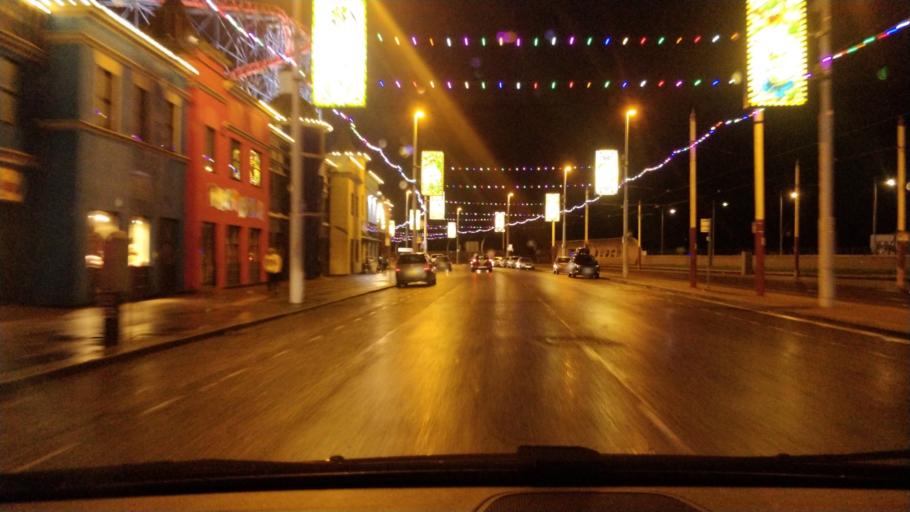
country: GB
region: England
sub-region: Blackpool
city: Blackpool
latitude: 53.7919
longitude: -3.0571
